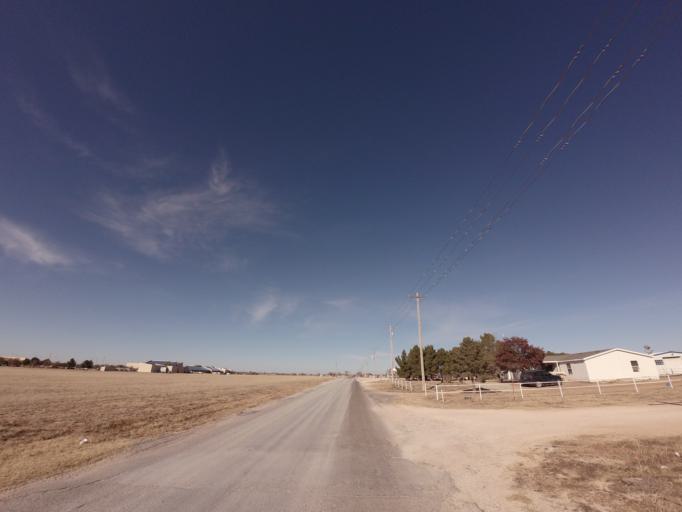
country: US
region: New Mexico
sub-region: Curry County
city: Clovis
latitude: 34.4000
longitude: -103.1612
